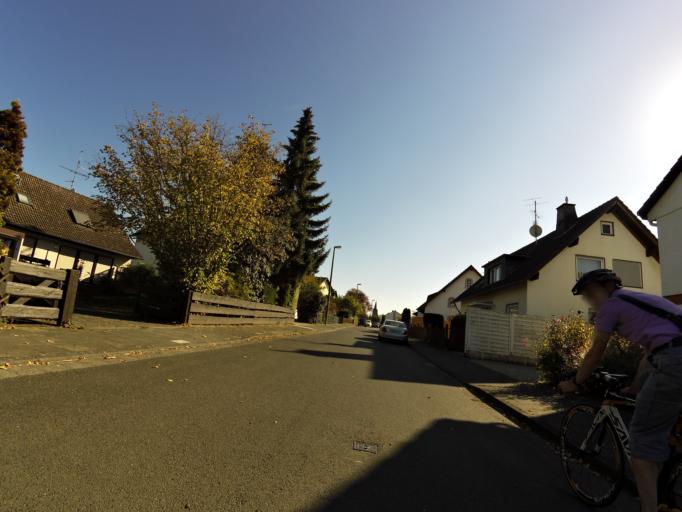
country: DE
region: North Rhine-Westphalia
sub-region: Regierungsbezirk Koln
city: Alfter
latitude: 50.6962
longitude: 7.0191
